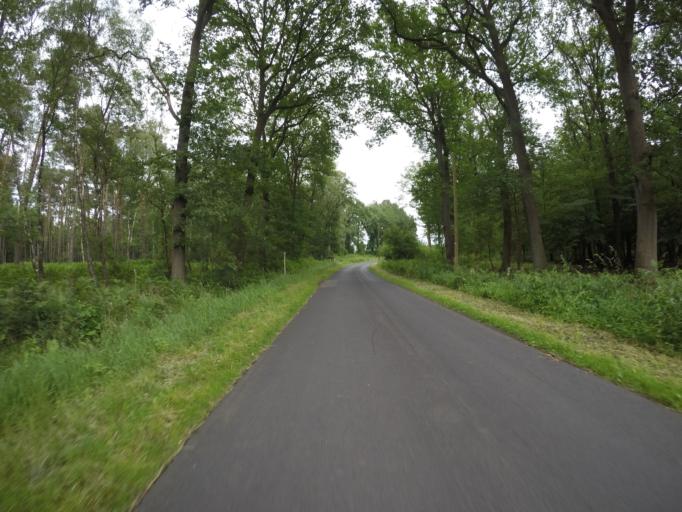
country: DE
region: North Rhine-Westphalia
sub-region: Regierungsbezirk Dusseldorf
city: Hunxe
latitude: 51.6196
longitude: 6.8266
